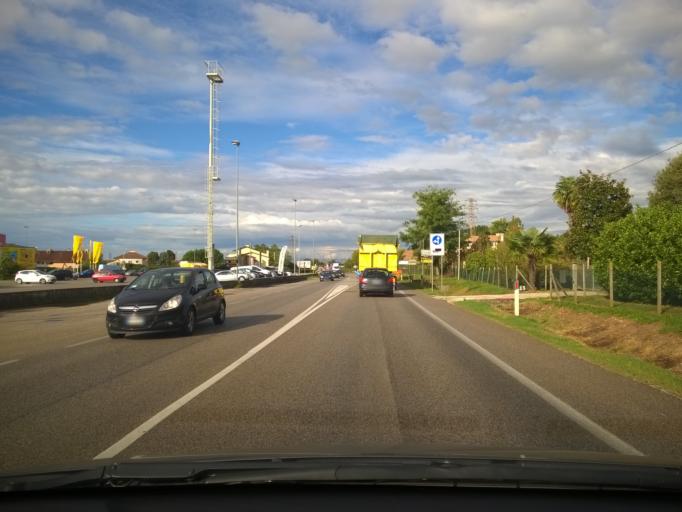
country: IT
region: Veneto
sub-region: Provincia di Treviso
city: Salvatronda
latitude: 45.6857
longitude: 11.9572
